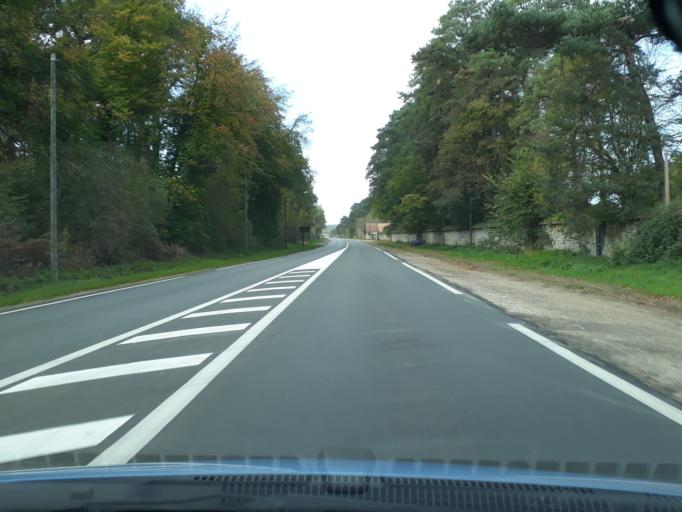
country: FR
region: Ile-de-France
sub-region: Departement de Seine-et-Marne
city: Fontainebleau
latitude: 48.3946
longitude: 2.6854
